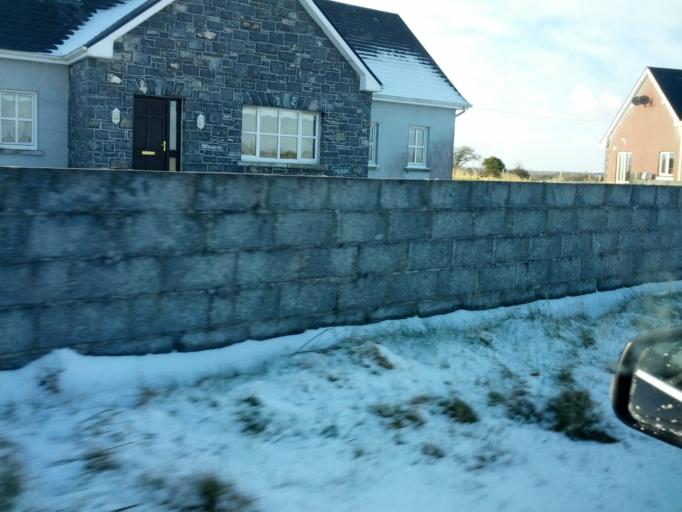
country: IE
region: Connaught
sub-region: County Galway
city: Oranmore
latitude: 53.1907
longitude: -8.8419
